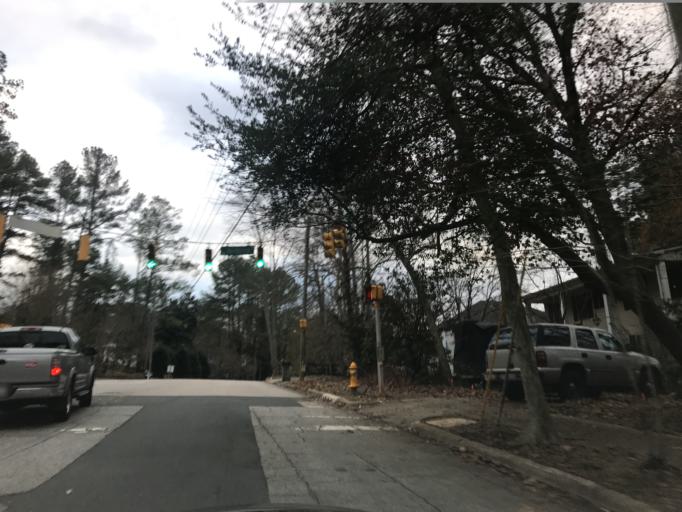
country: US
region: North Carolina
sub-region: Wake County
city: West Raleigh
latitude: 35.8444
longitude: -78.6613
